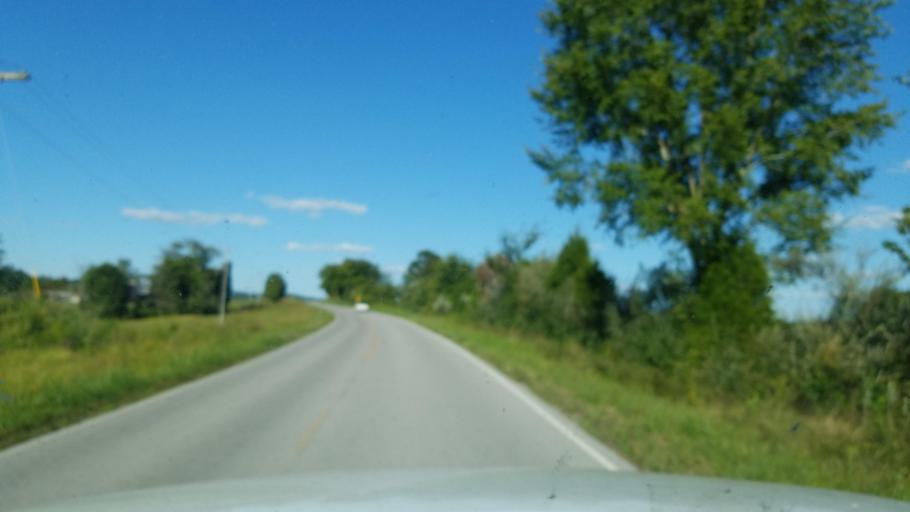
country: US
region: Illinois
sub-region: Hardin County
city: Rosiclare
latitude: 37.5686
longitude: -88.4015
